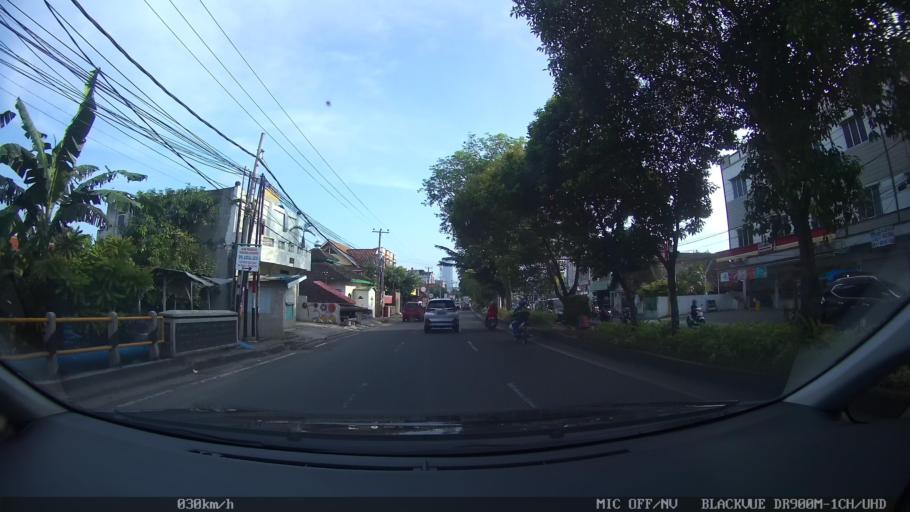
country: ID
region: Lampung
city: Kedaton
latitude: -5.3993
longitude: 105.2613
